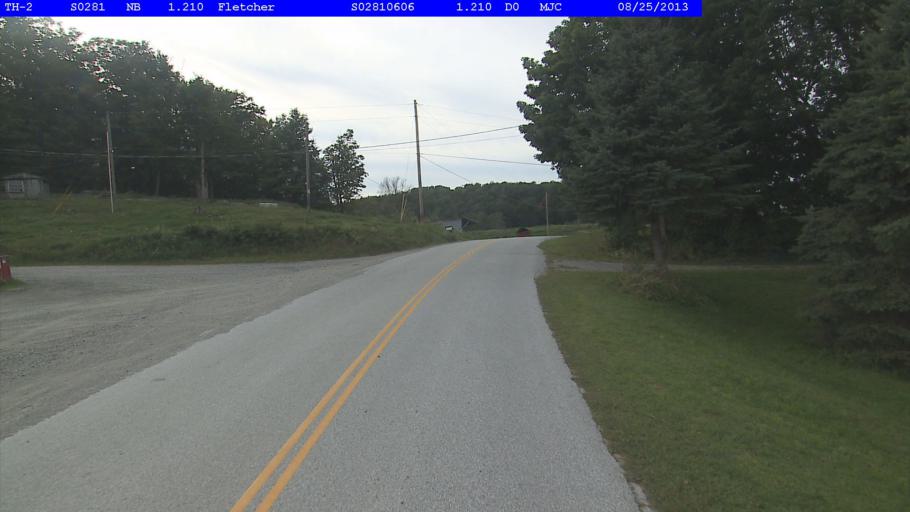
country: US
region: Vermont
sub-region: Chittenden County
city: Milton
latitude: 44.6936
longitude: -72.9316
